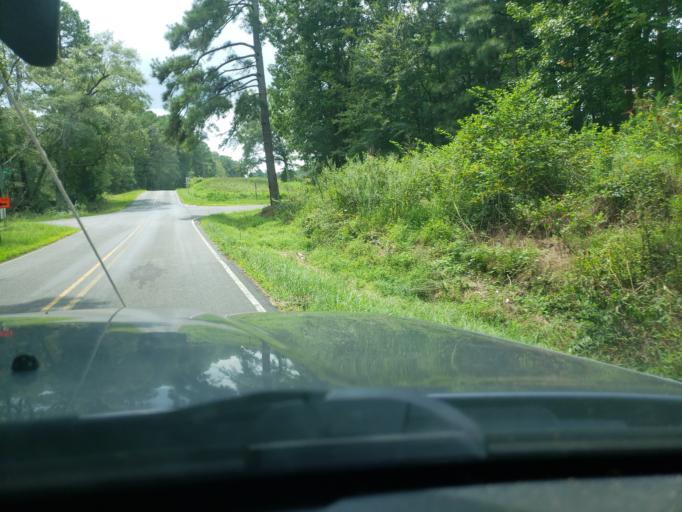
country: US
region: North Carolina
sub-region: Wake County
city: Zebulon
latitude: 35.8967
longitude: -78.3354
